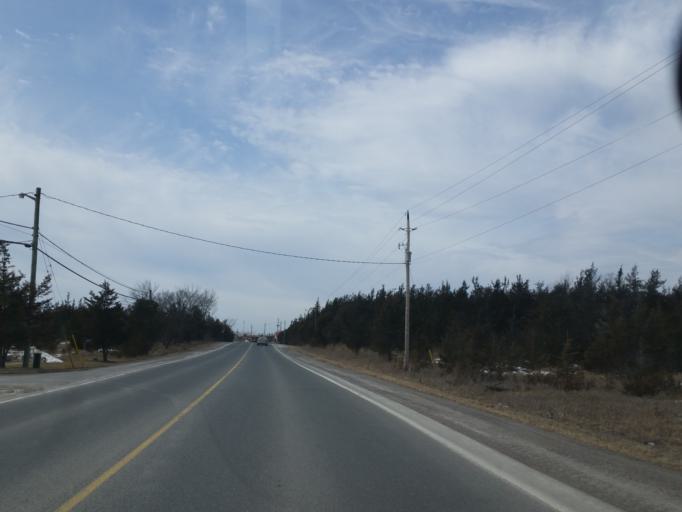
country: CA
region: Ontario
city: Belleville
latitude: 44.1969
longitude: -77.2373
